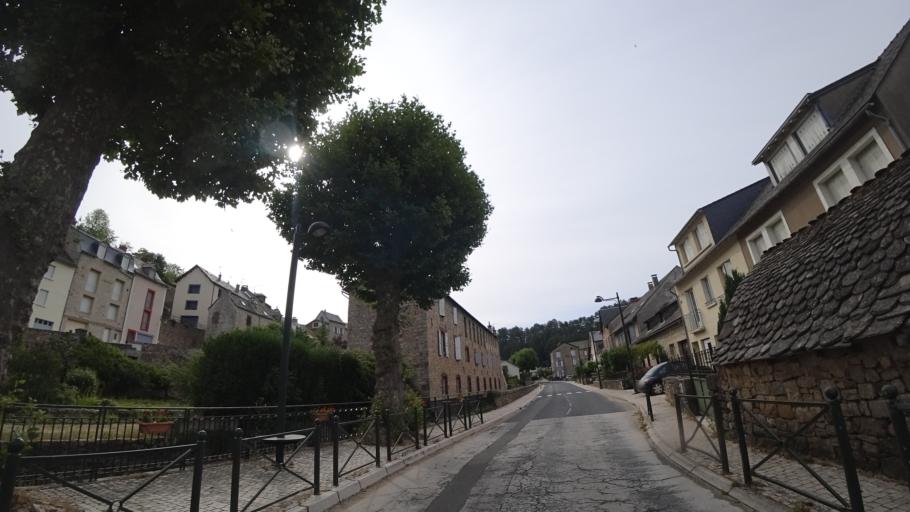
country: FR
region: Languedoc-Roussillon
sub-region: Departement de la Lozere
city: La Canourgue
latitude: 44.4304
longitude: 3.2162
